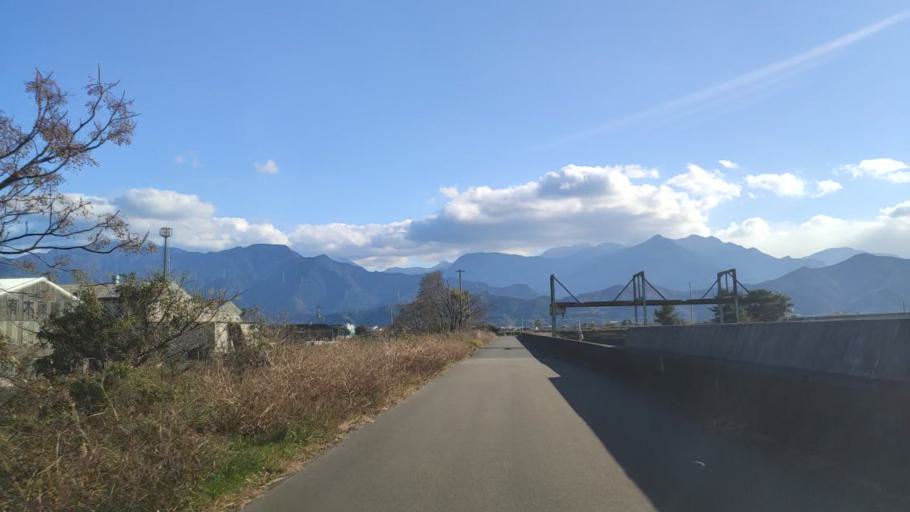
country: JP
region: Ehime
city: Saijo
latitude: 33.9220
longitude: 133.1558
